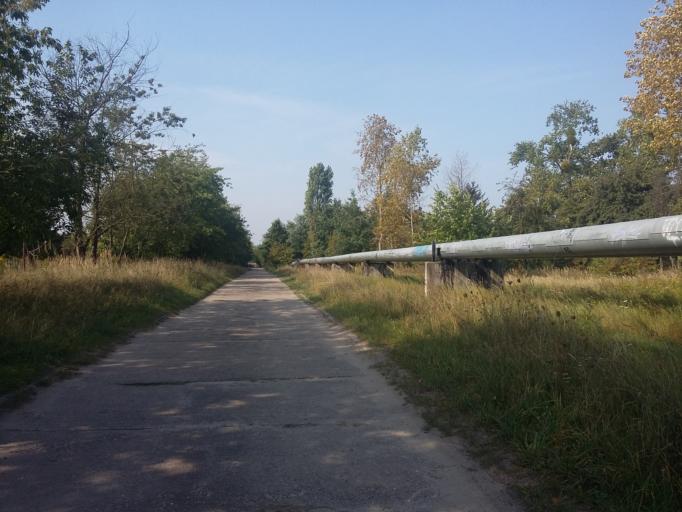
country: PL
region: Lodz Voivodeship
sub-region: Powiat pabianicki
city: Ksawerow
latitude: 51.7361
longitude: 19.3937
